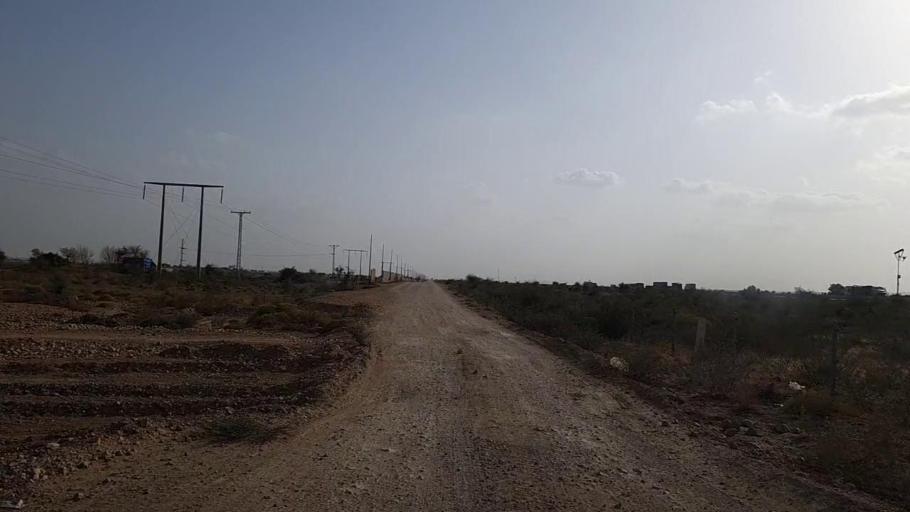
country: PK
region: Sindh
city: Kotri
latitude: 25.2297
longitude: 67.9271
